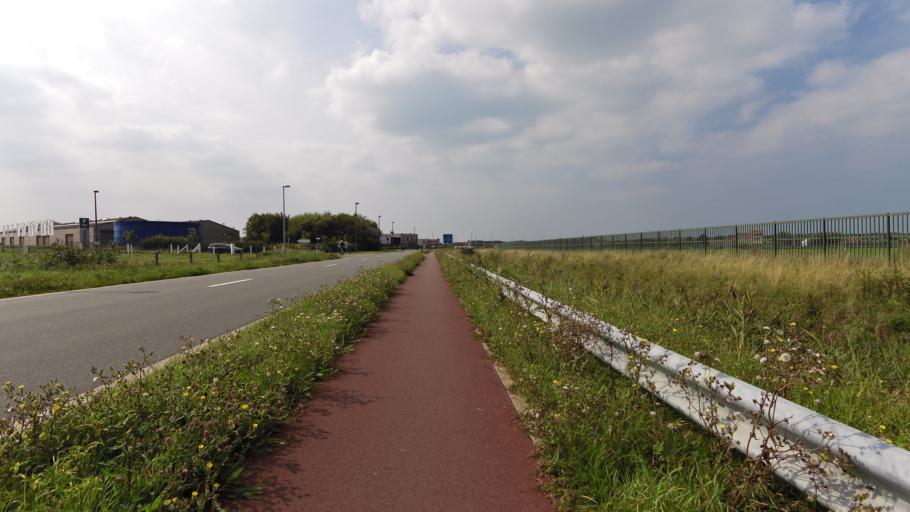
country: BE
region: Flanders
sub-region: Provincie West-Vlaanderen
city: Middelkerke
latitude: 51.1943
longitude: 2.8480
